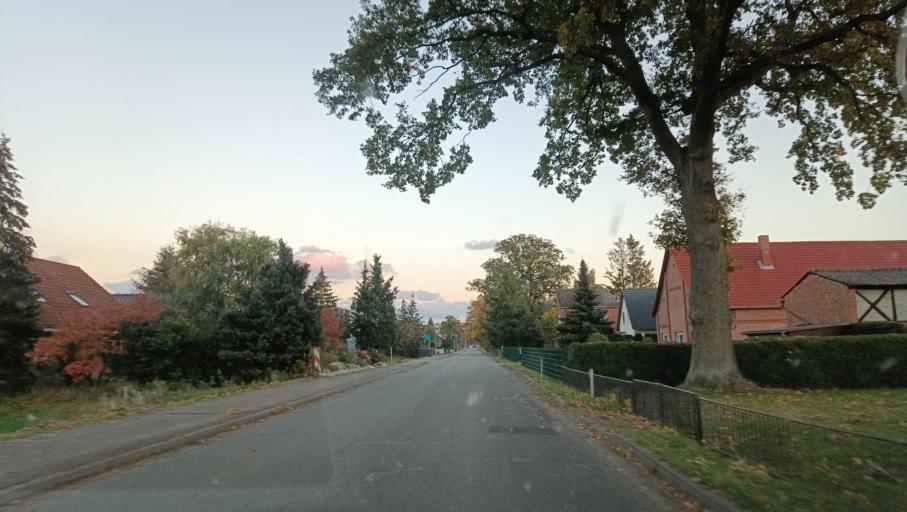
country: DE
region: Mecklenburg-Vorpommern
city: Ludwigslust
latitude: 53.2803
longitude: 11.4909
